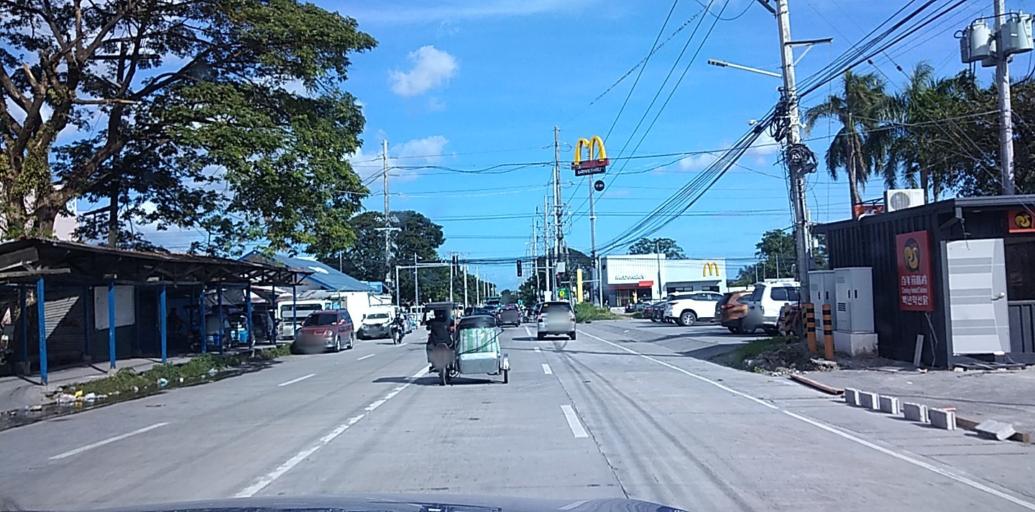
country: PH
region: Central Luzon
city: Santol
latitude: 15.1443
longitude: 120.5585
